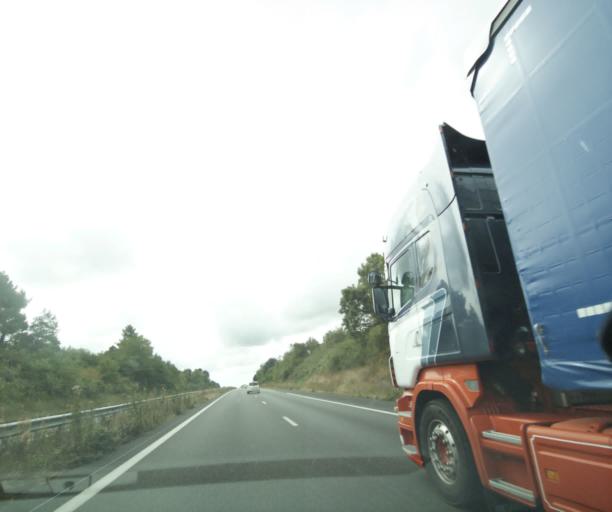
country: FR
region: Poitou-Charentes
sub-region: Departement de la Charente-Maritime
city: Mirambeau
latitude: 45.4026
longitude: -0.6024
